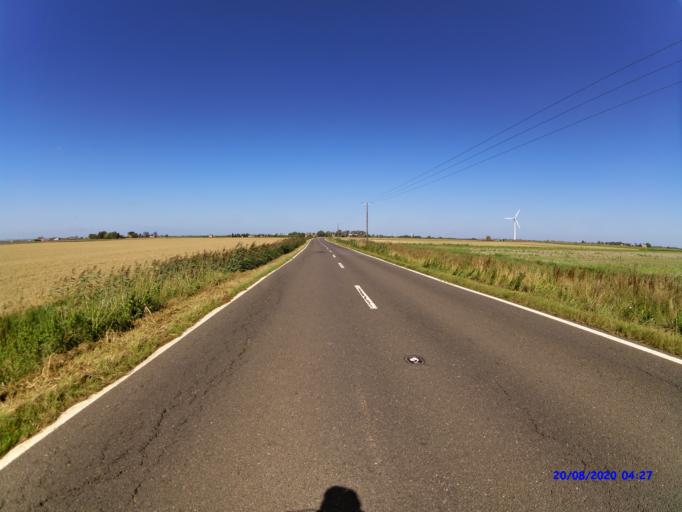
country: GB
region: England
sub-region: Cambridgeshire
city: Whittlesey
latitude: 52.5038
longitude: -0.1335
